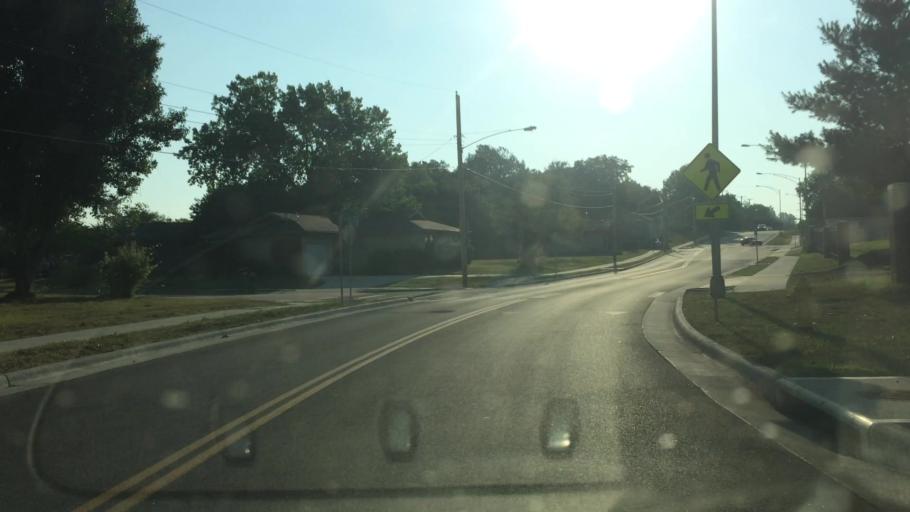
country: US
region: Missouri
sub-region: Greene County
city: Springfield
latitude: 37.2186
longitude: -93.2797
